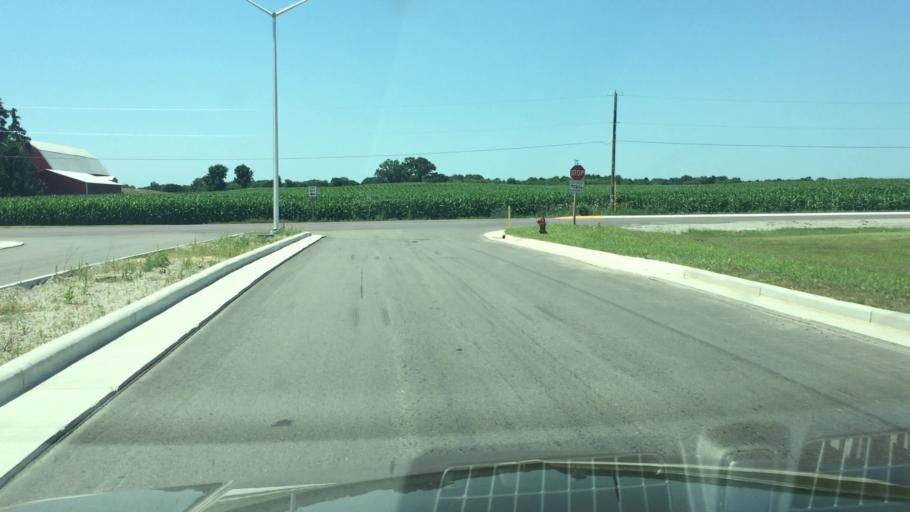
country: US
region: Wisconsin
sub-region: Fond du Lac County
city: Waupun
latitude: 43.6081
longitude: -88.7241
